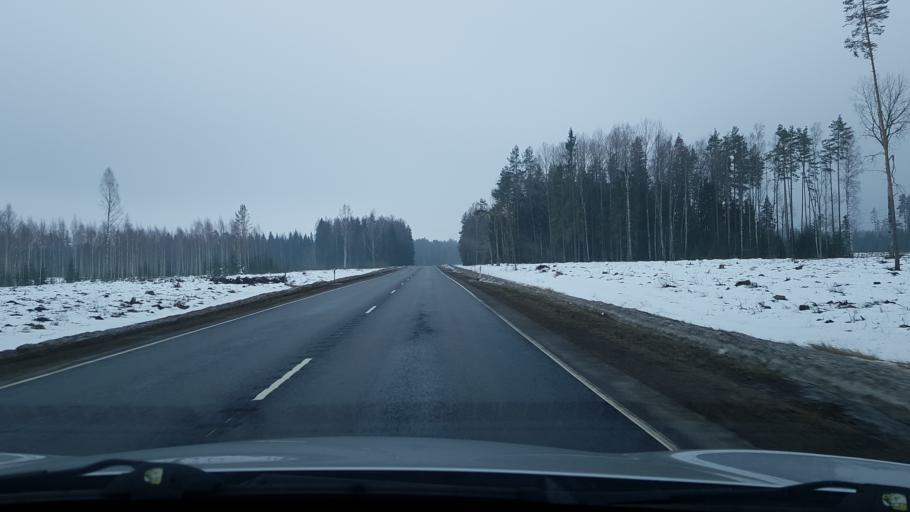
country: EE
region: Valgamaa
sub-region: Valga linn
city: Valga
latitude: 57.8914
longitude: 26.1655
